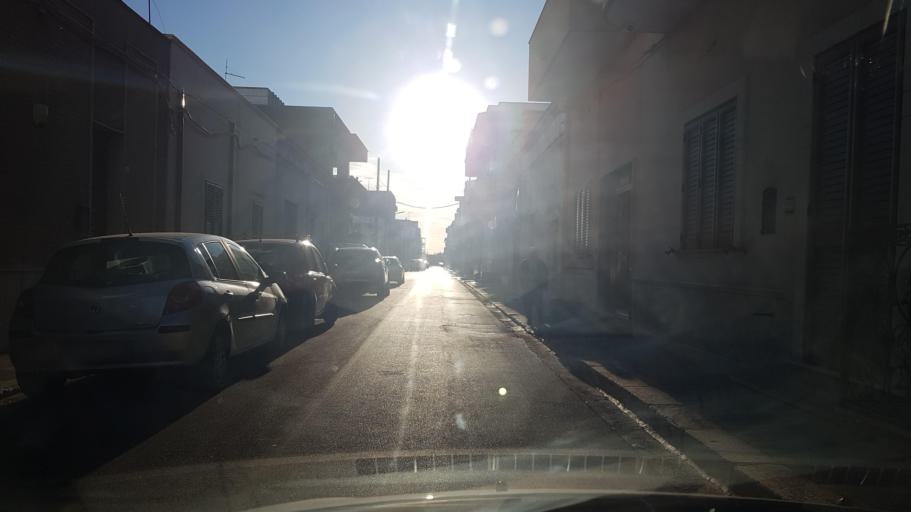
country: IT
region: Apulia
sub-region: Provincia di Brindisi
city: San Pancrazio Salentino
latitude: 40.4168
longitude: 17.8333
